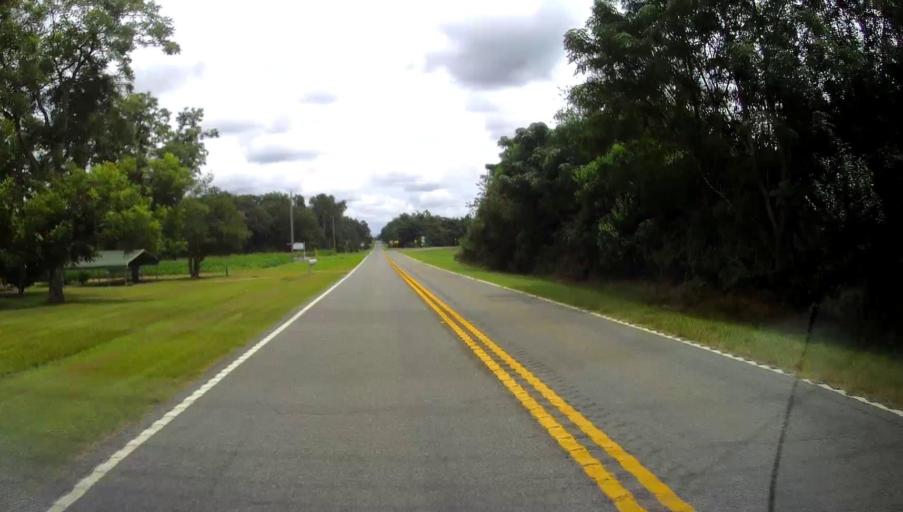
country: US
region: Georgia
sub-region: Dooly County
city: Unadilla
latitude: 32.2586
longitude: -83.7786
